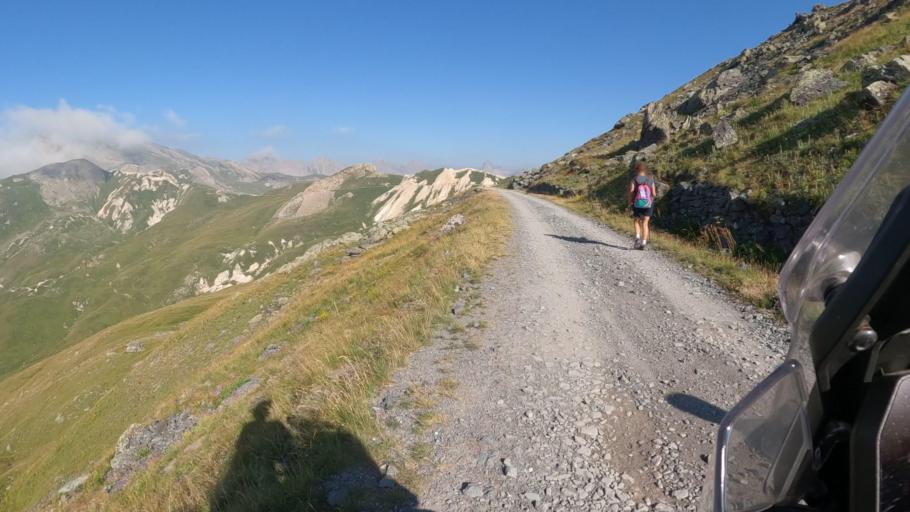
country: IT
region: Piedmont
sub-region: Provincia di Cuneo
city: Sambuco
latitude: 44.3839
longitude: 7.0757
